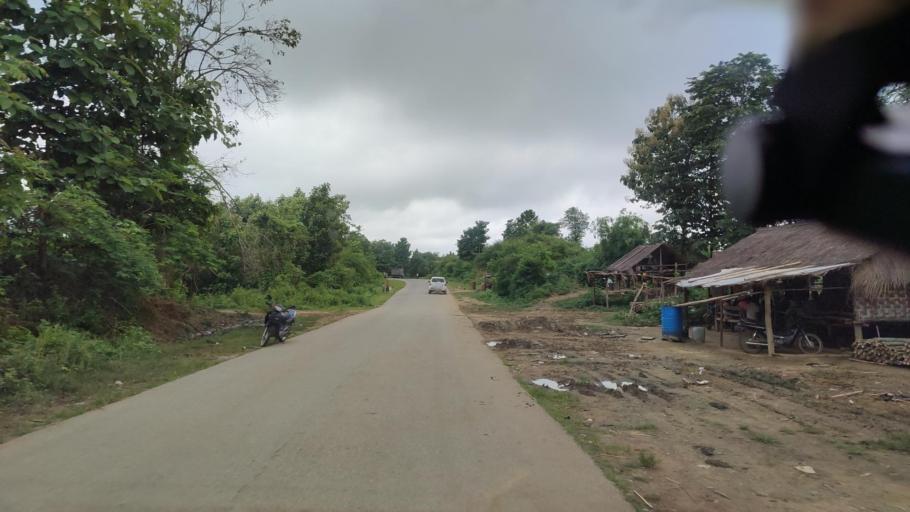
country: MM
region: Mandalay
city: Nay Pyi Taw
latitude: 19.9967
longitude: 95.9250
